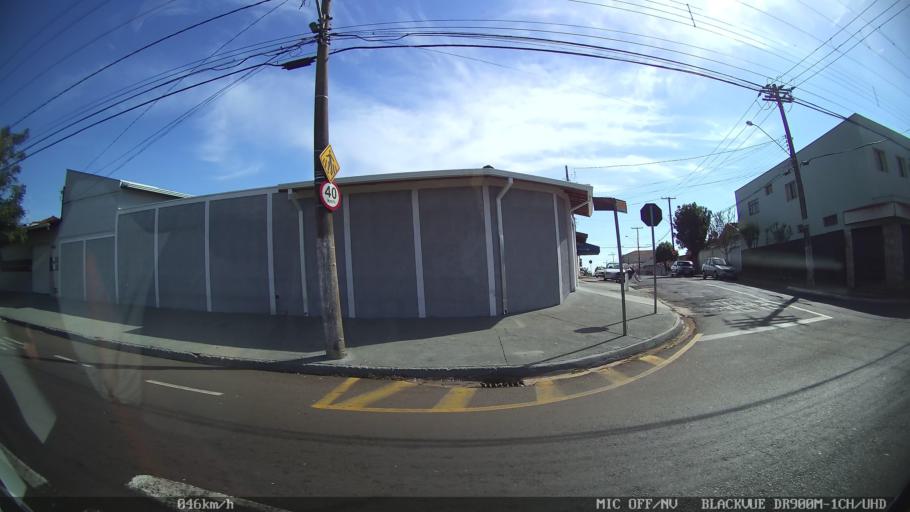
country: BR
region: Sao Paulo
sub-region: Franca
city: Franca
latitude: -20.5021
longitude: -47.3990
